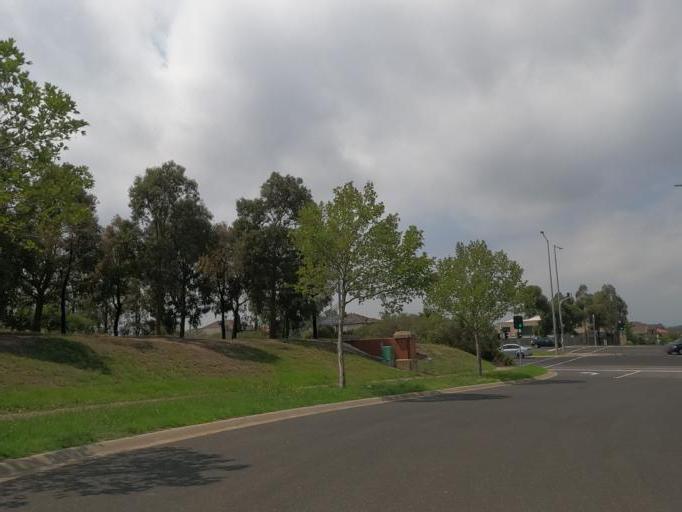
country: AU
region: Victoria
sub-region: Hume
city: Attwood
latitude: -37.6697
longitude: 144.8846
